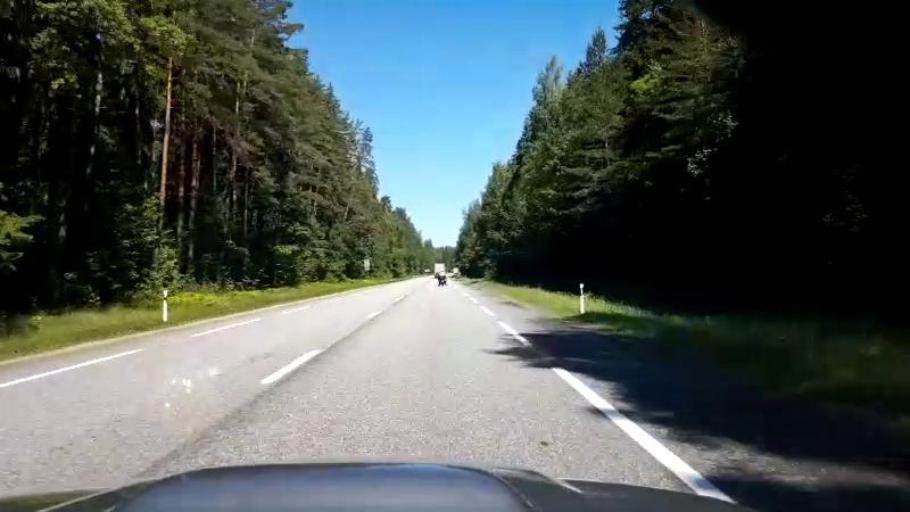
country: LV
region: Saulkrastu
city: Saulkrasti
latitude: 57.3969
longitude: 24.4282
